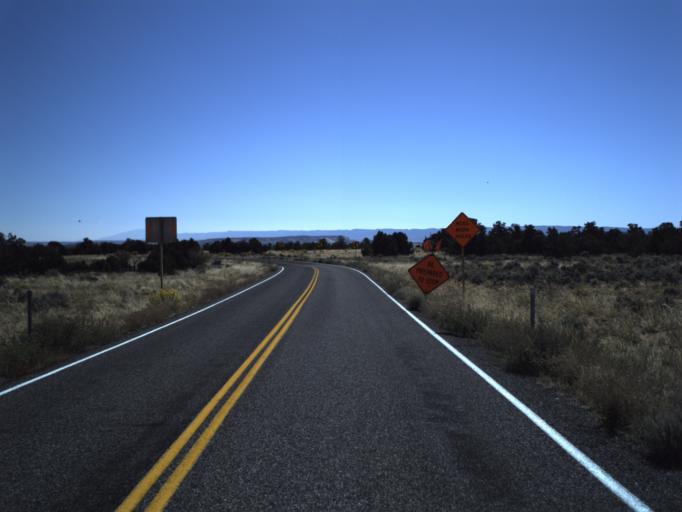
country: US
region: Utah
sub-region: Wayne County
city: Loa
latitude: 37.8468
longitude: -111.4277
